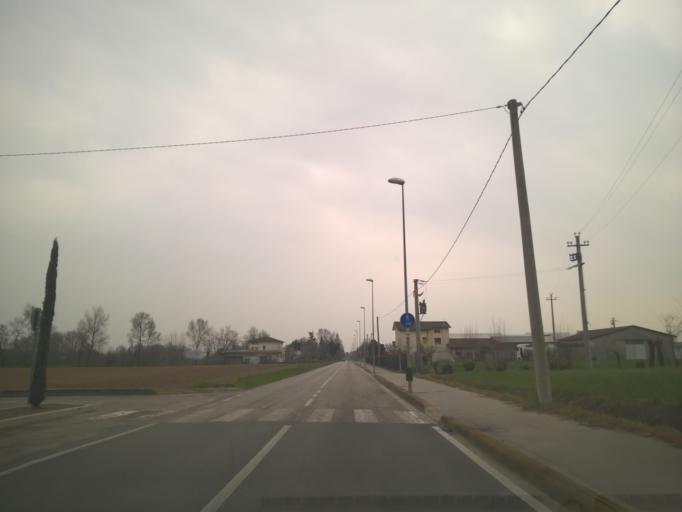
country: IT
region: Veneto
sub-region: Provincia di Vicenza
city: Sandrigo
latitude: 45.6477
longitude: 11.6059
